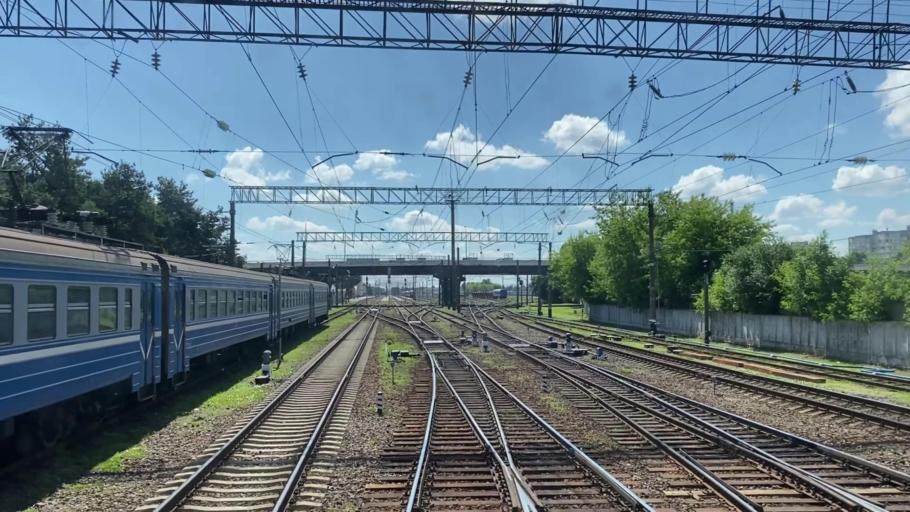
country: BY
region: Brest
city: Baranovichi
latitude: 53.1335
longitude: 26.0375
